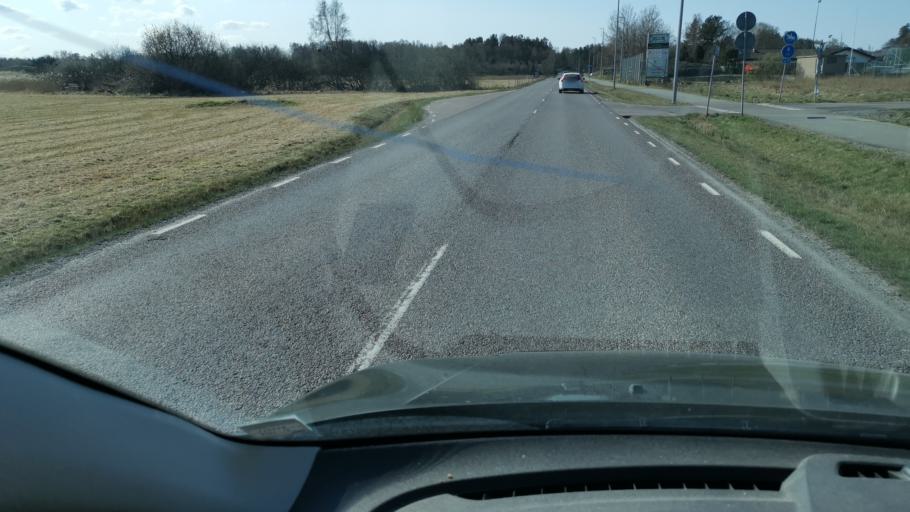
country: SE
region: Vaestra Goetaland
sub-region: Goteborg
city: Torslanda
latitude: 57.7529
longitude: 11.8297
